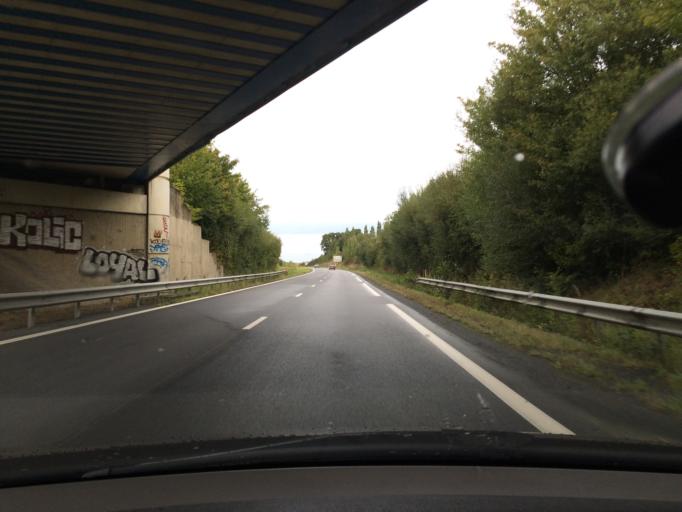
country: FR
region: Brittany
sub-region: Departement d'Ille-et-Vilaine
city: Janze
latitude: 47.9667
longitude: -1.5289
